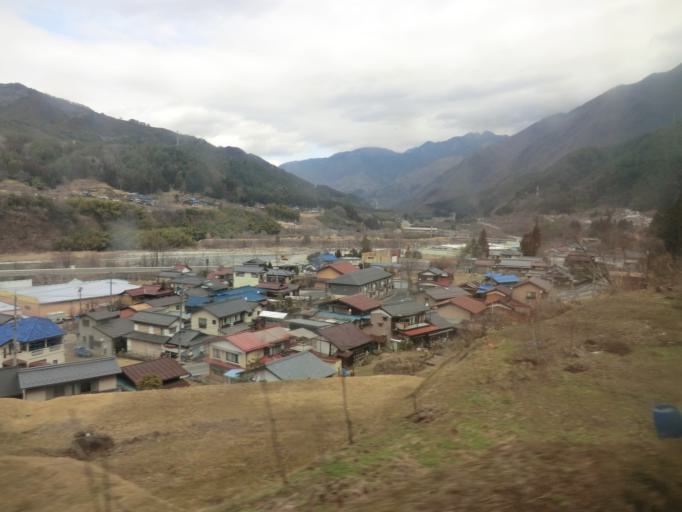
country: JP
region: Nagano
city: Iida
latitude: 35.6945
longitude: 137.6860
